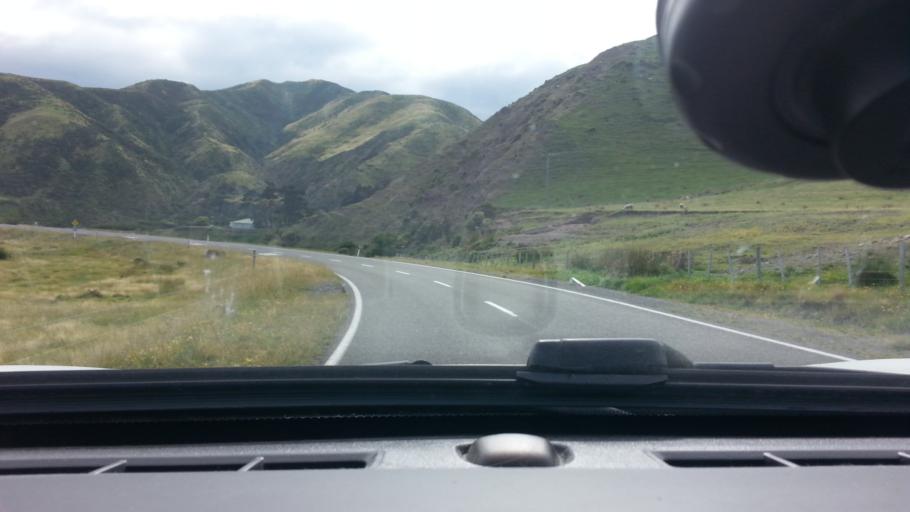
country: NZ
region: Wellington
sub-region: South Wairarapa District
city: Waipawa
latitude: -41.5526
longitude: 175.2252
